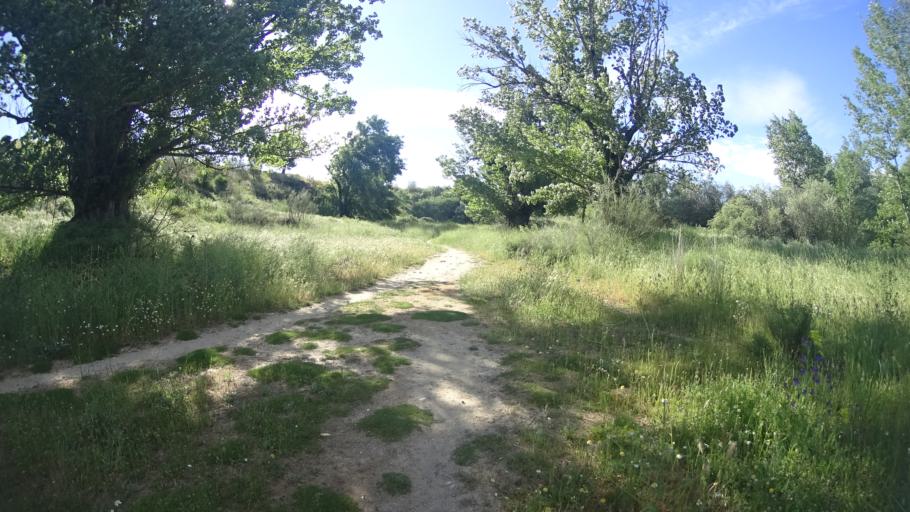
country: ES
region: Madrid
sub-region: Provincia de Madrid
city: Villanueva del Pardillo
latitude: 40.5126
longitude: -3.9383
